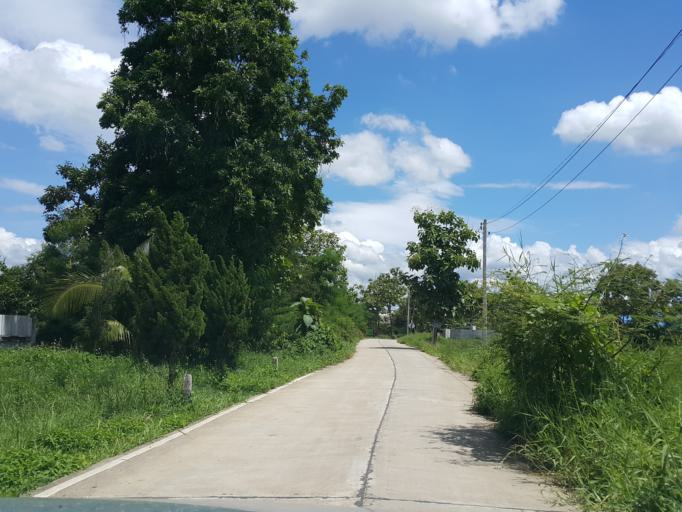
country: TH
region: Chiang Mai
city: San Kamphaeng
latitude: 18.7659
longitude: 99.1010
